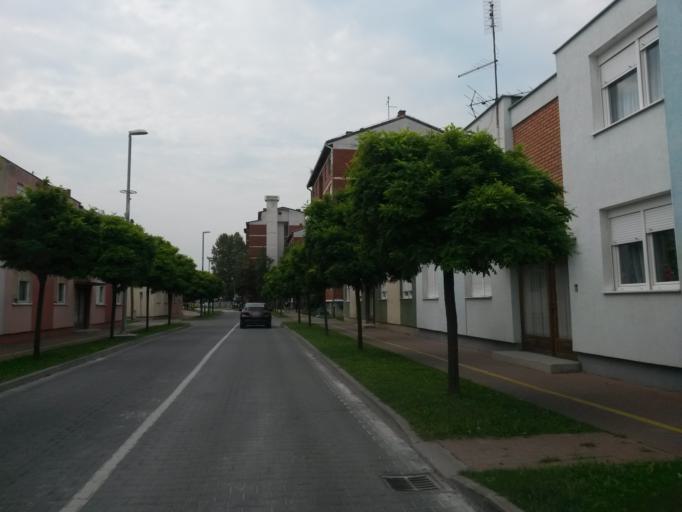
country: HR
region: Osjecko-Baranjska
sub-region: Grad Osijek
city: Osijek
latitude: 45.5433
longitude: 18.7147
